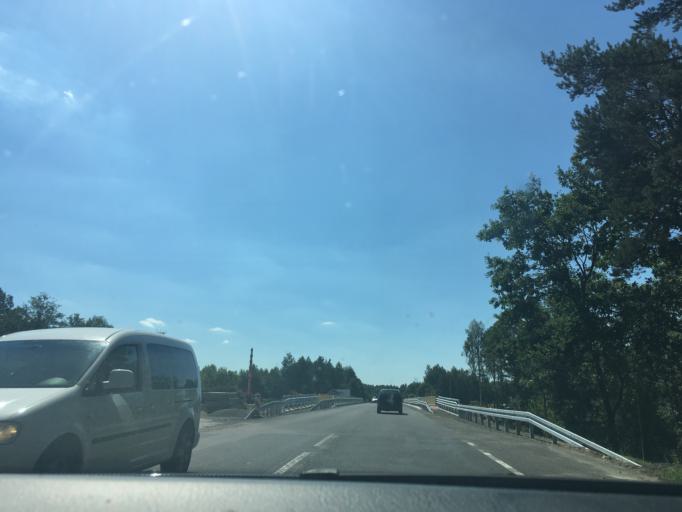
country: PL
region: Subcarpathian Voivodeship
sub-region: Powiat nizanski
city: Jarocin
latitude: 50.6223
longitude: 22.2865
